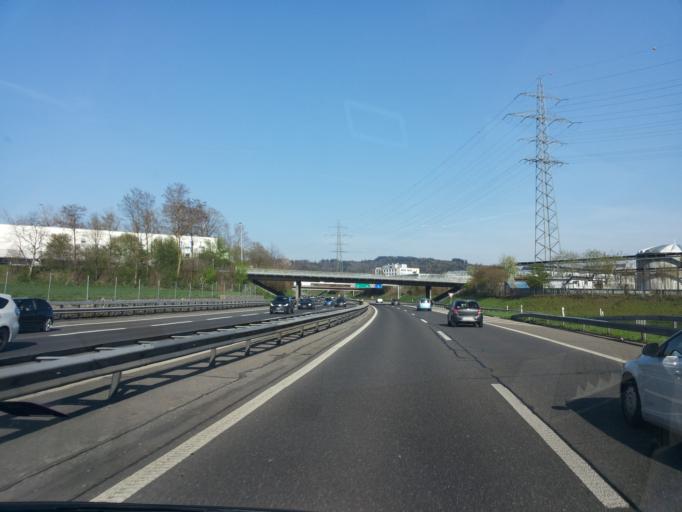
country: CH
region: Aargau
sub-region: Bezirk Zofingen
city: Oftringen
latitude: 47.3044
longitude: 7.9203
